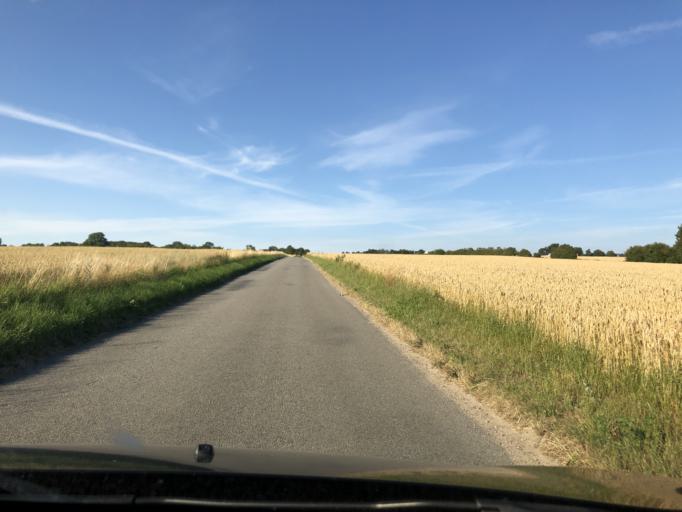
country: DK
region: South Denmark
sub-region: AEro Kommune
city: AEroskobing
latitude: 54.8591
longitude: 10.3650
